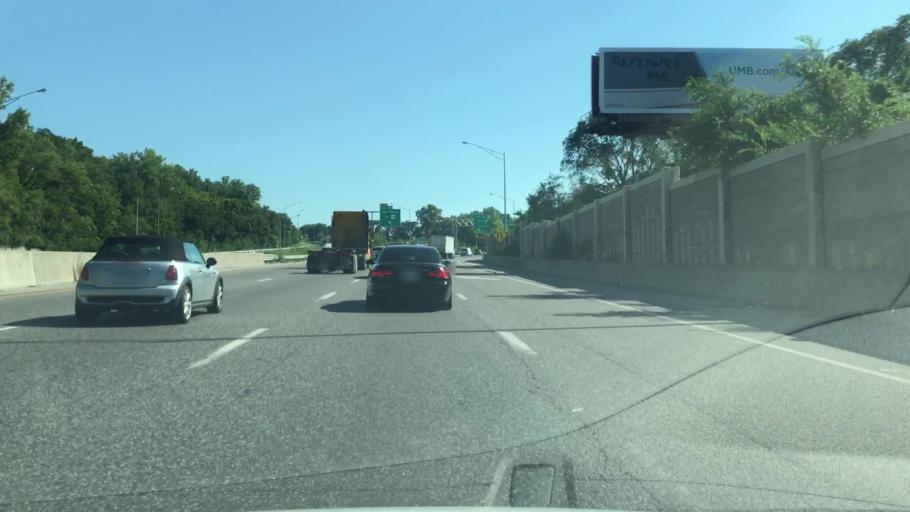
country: US
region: Missouri
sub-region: Clay County
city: North Kansas City
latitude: 39.1131
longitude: -94.5648
